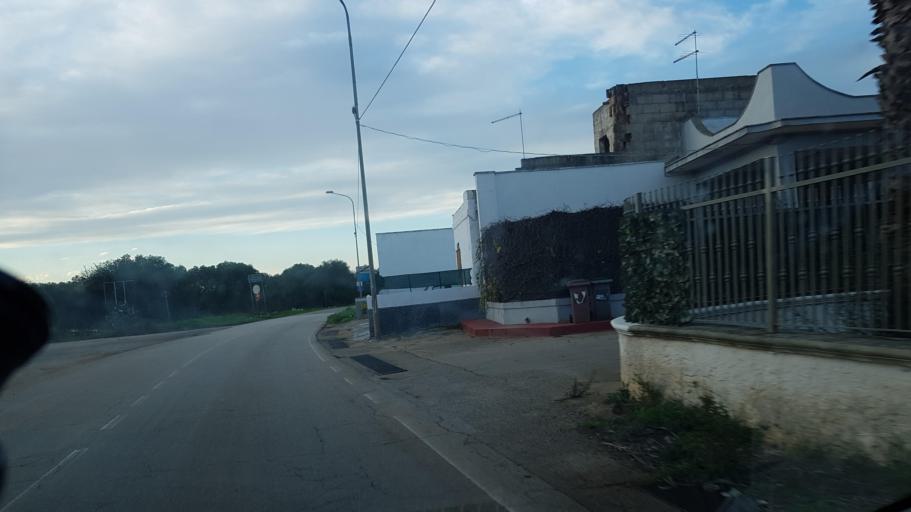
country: IT
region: Apulia
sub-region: Provincia di Brindisi
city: San Vito dei Normanni
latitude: 40.6495
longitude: 17.6944
